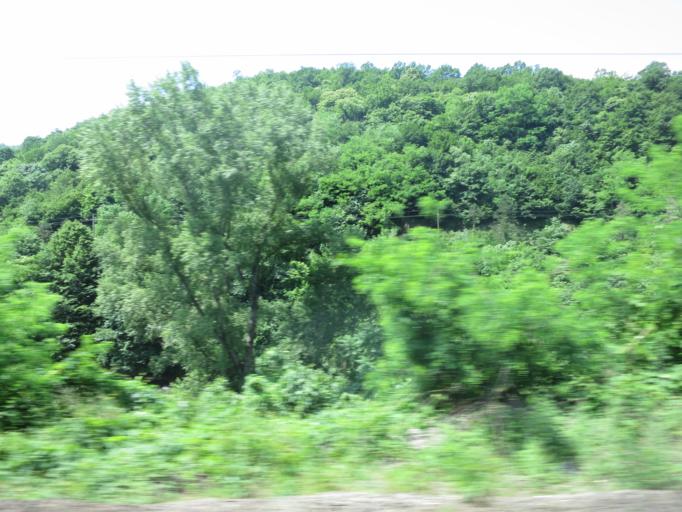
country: GE
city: Shorapani
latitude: 42.0900
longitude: 43.1412
